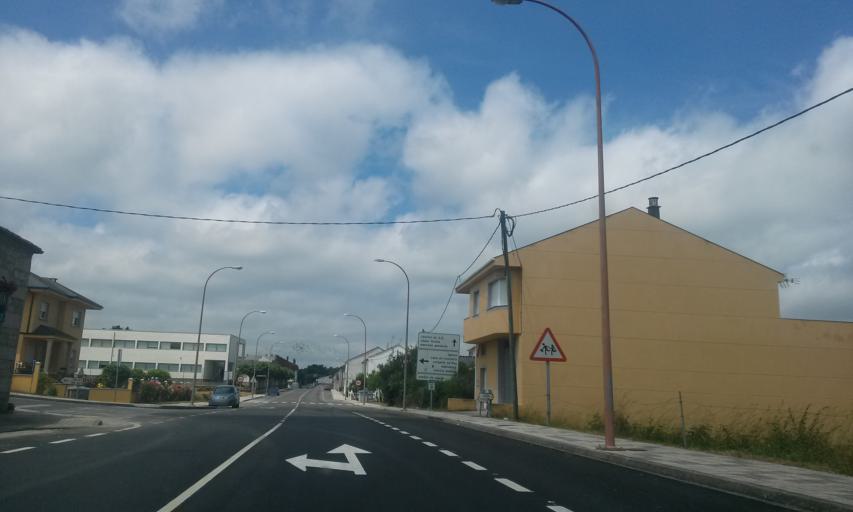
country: ES
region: Galicia
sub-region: Provincia de Lugo
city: Friol
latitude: 43.0299
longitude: -7.7880
